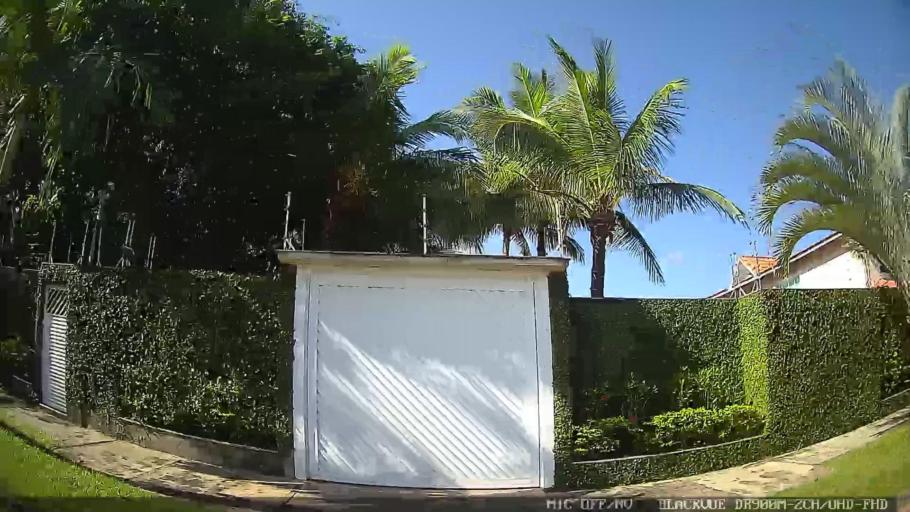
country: BR
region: Sao Paulo
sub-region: Peruibe
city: Peruibe
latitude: -24.2828
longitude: -46.9583
